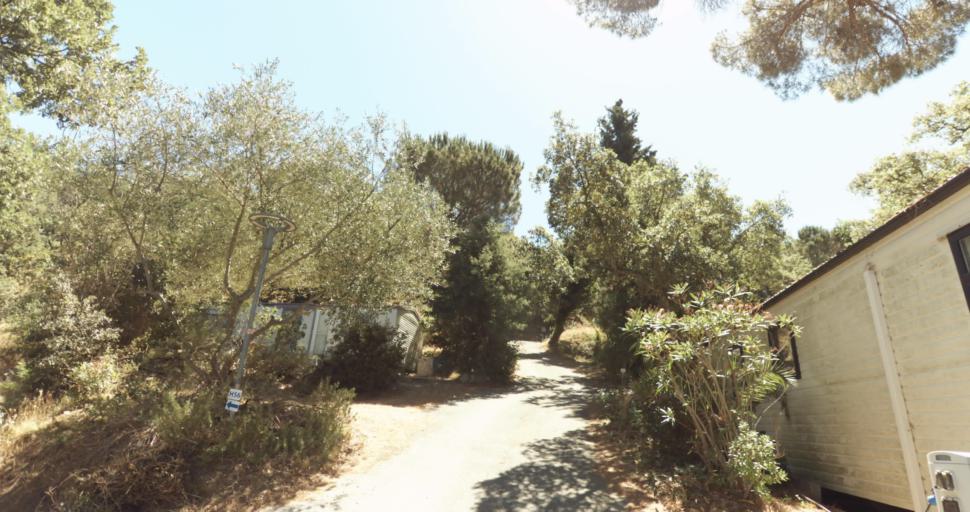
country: FR
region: Provence-Alpes-Cote d'Azur
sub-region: Departement du Var
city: Gassin
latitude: 43.2402
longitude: 6.5787
